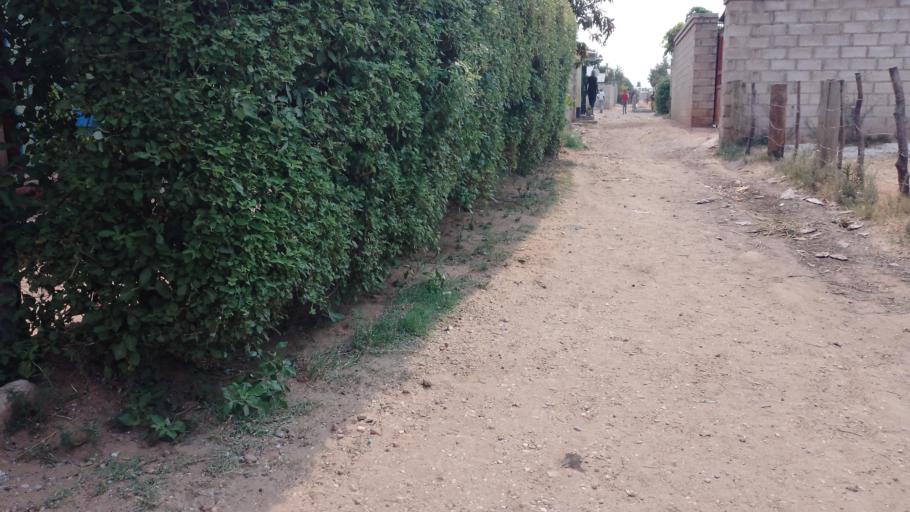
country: ZM
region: Lusaka
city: Lusaka
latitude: -15.4070
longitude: 28.3747
